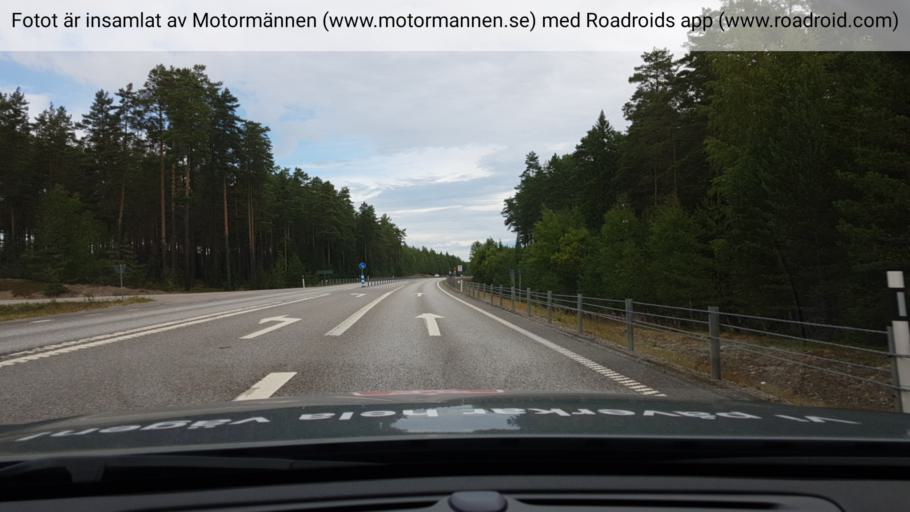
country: SE
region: Uppsala
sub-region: Heby Kommun
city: Tarnsjo
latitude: 60.1908
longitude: 16.9453
